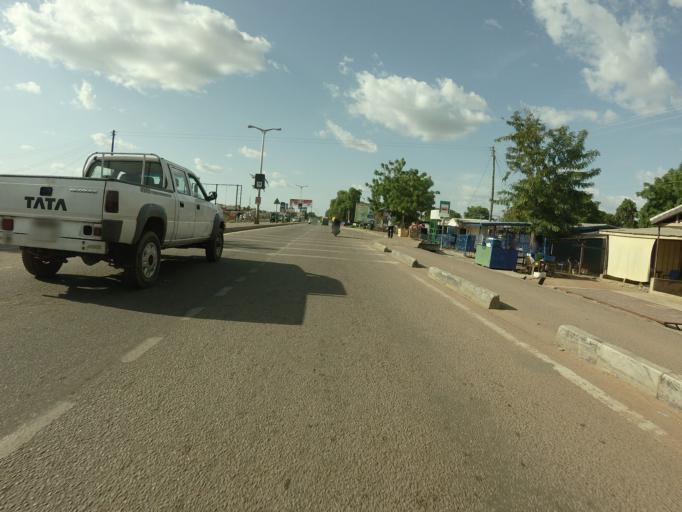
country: GH
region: Upper East
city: Bolgatanga
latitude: 10.7756
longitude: -0.8552
